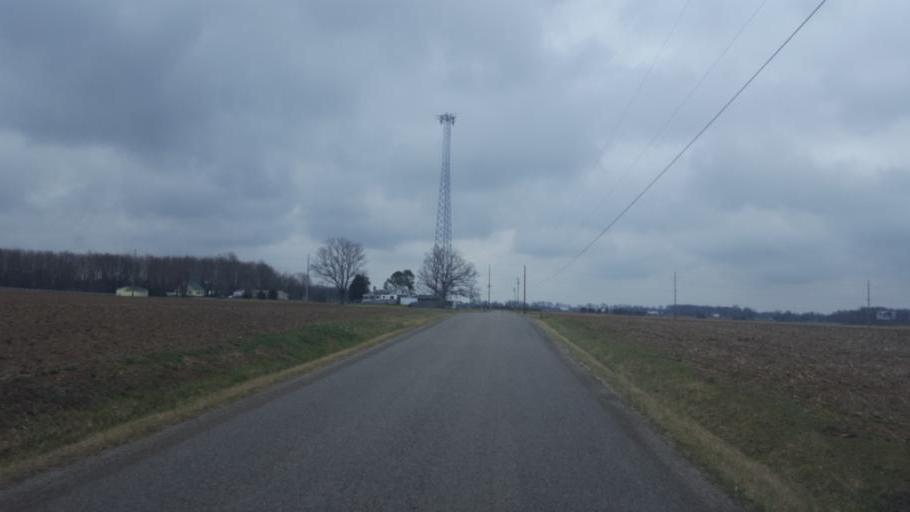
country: US
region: Ohio
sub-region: Delaware County
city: Ashley
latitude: 40.3612
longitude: -82.8553
